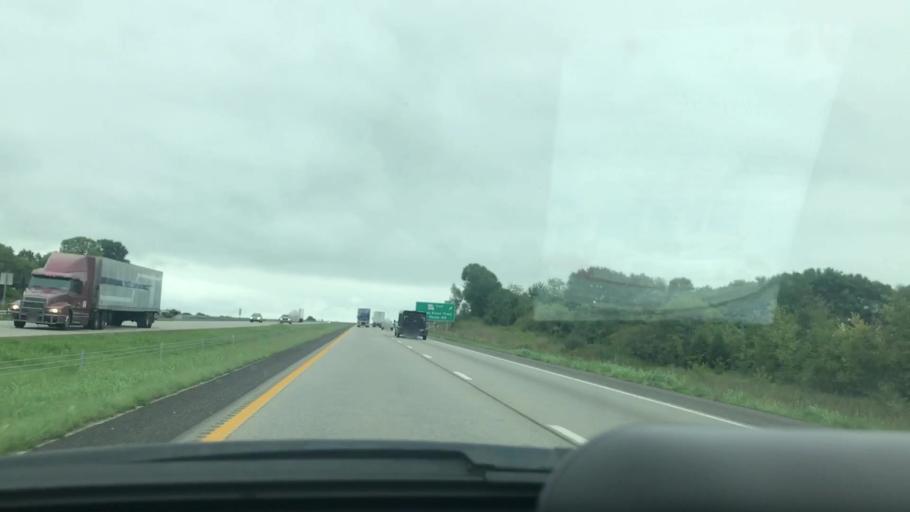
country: US
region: Missouri
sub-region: Greene County
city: Republic
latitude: 37.1941
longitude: -93.4535
